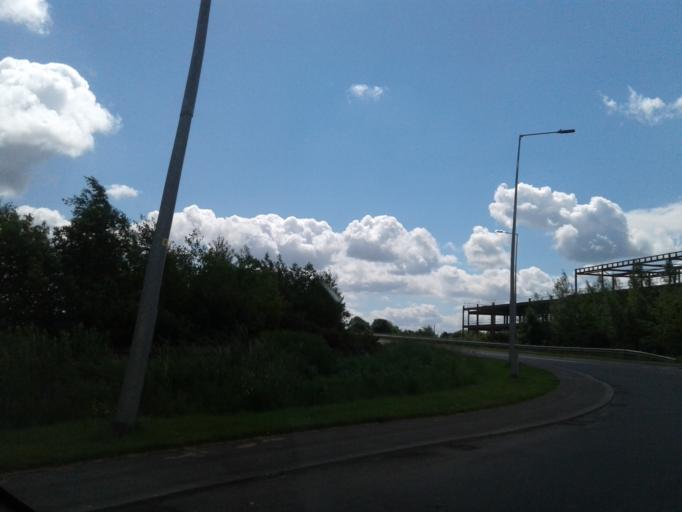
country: IE
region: Leinster
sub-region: Uibh Fhaili
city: Tullamore
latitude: 53.2882
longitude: -7.4832
